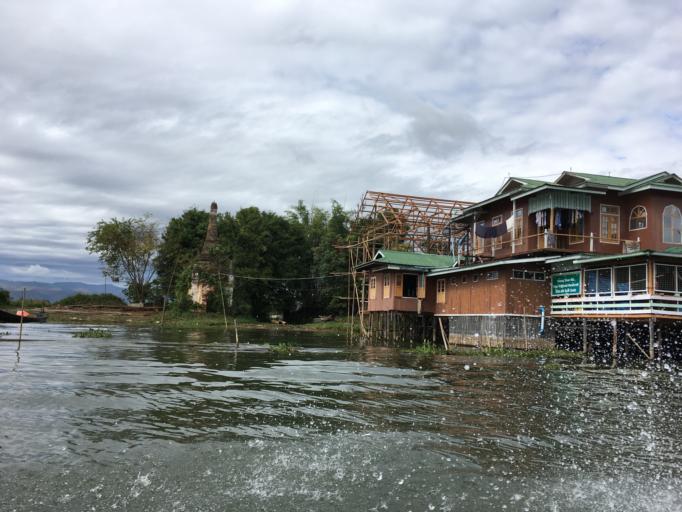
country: MM
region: Shan
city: Taunggyi
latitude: 20.4534
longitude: 96.9068
